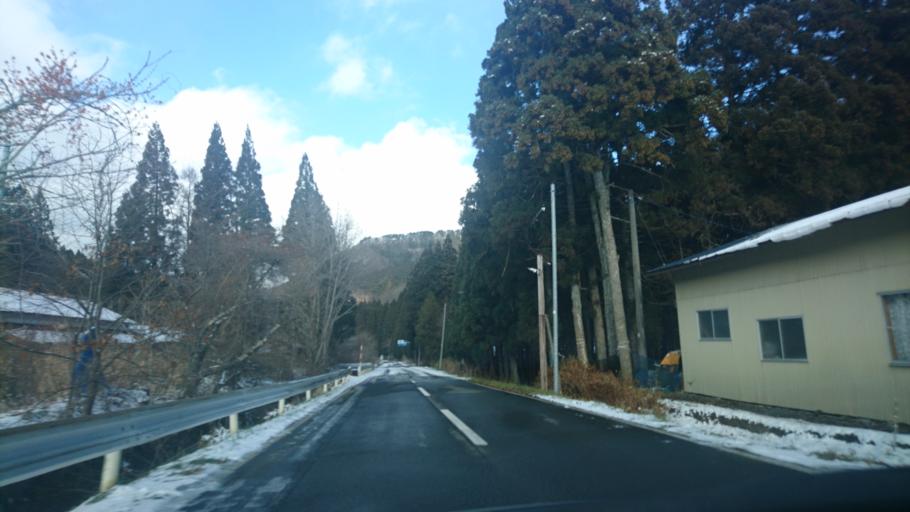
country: JP
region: Iwate
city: Tono
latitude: 39.1622
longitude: 141.3655
